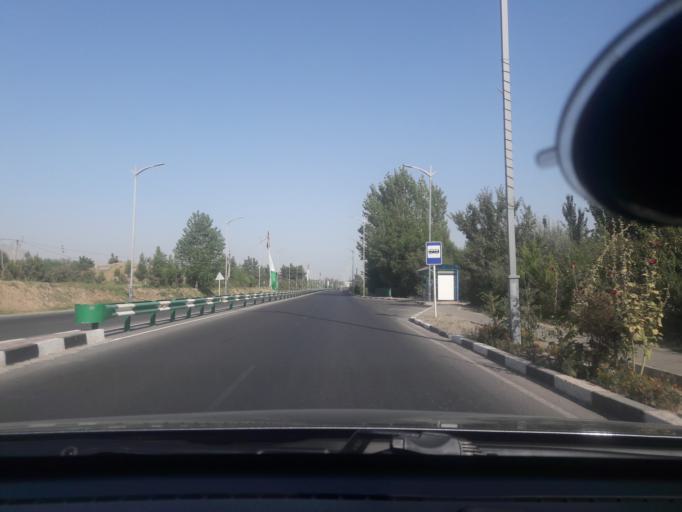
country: TJ
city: Shahrinav
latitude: 38.5762
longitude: 68.3418
